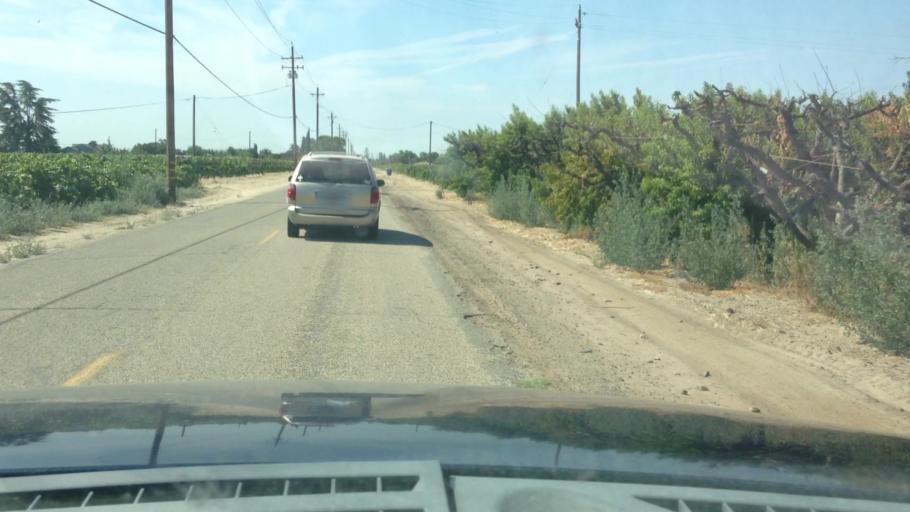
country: US
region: California
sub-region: Fresno County
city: Kingsburg
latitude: 36.5436
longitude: -119.5566
